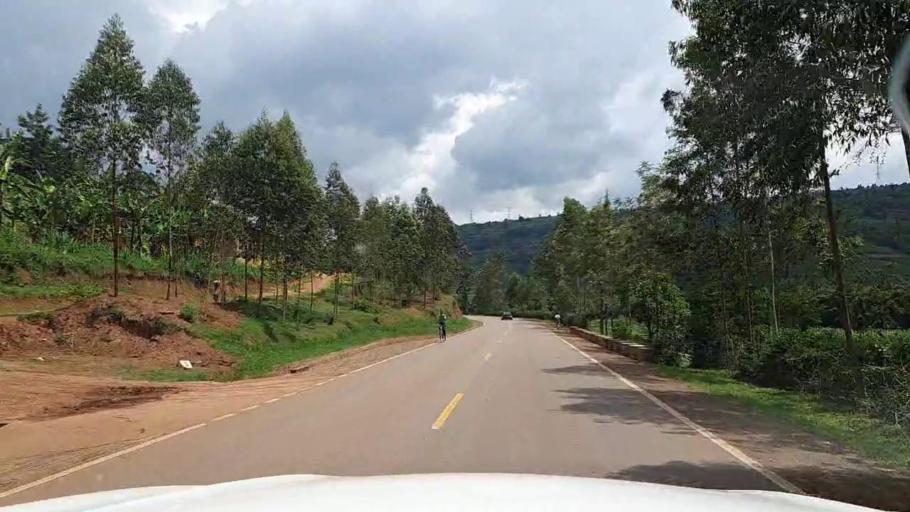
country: RW
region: Kigali
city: Kigali
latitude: -1.8035
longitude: 30.1270
